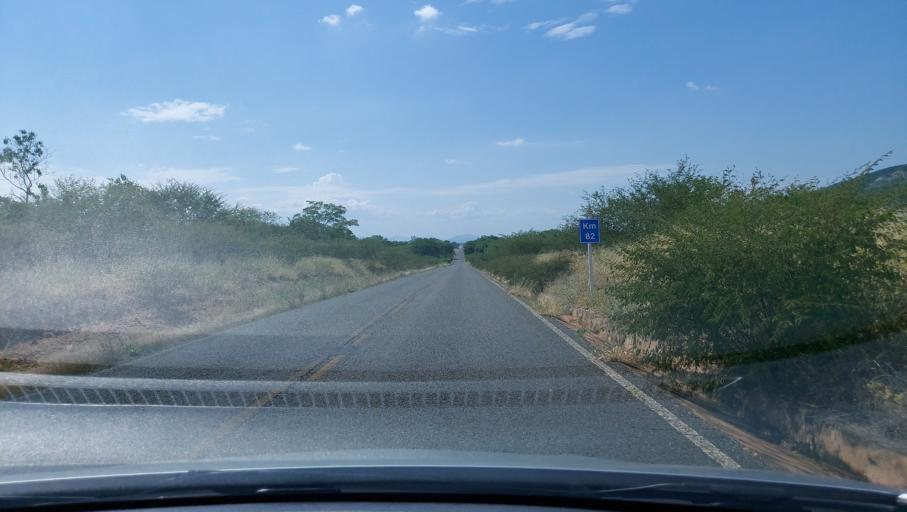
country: BR
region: Bahia
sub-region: Oliveira Dos Brejinhos
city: Beira Rio
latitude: -12.1654
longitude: -42.5479
